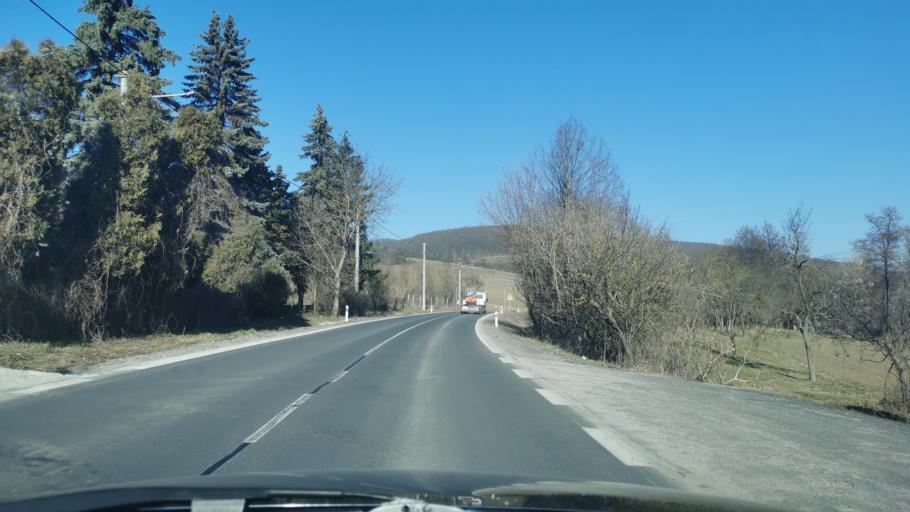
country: SK
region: Trnavsky
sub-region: Okres Senica
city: Senica
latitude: 48.7418
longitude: 17.4392
